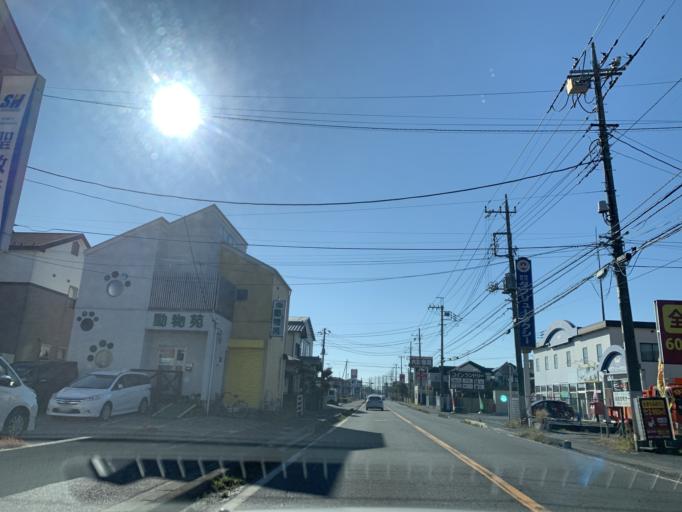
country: JP
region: Chiba
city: Matsudo
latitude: 35.8081
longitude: 139.8951
